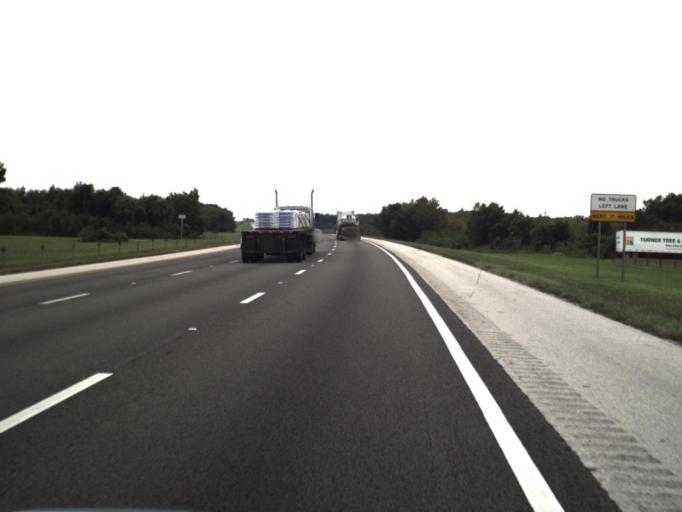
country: US
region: Florida
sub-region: Manatee County
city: Ellenton
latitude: 27.5662
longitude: -82.5147
